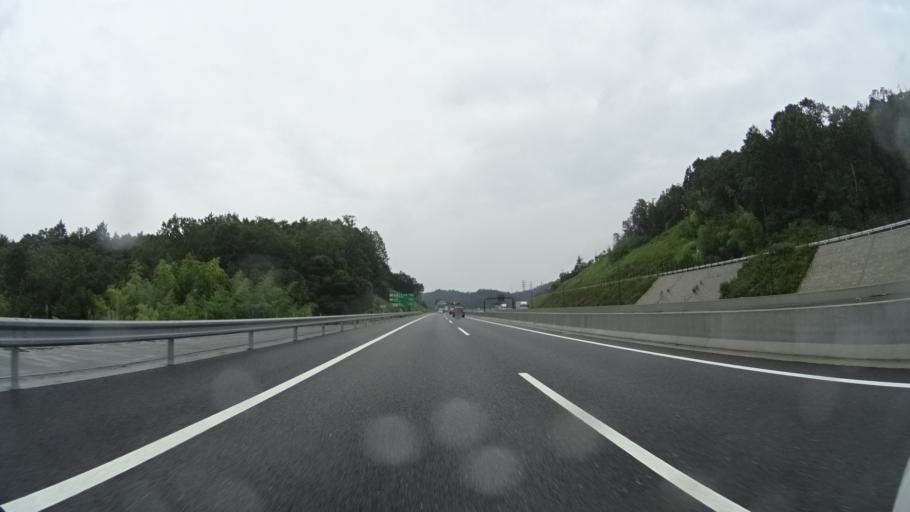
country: JP
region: Osaka
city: Ibaraki
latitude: 34.8779
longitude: 135.5272
